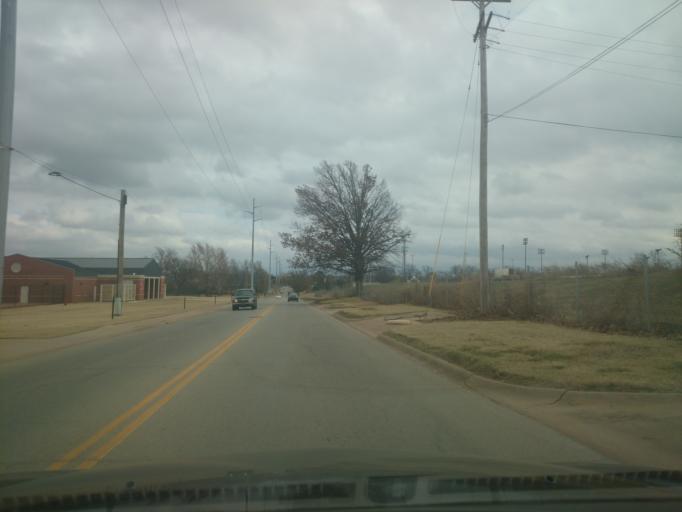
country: US
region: Oklahoma
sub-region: Payne County
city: Stillwater
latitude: 36.1305
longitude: -97.0671
